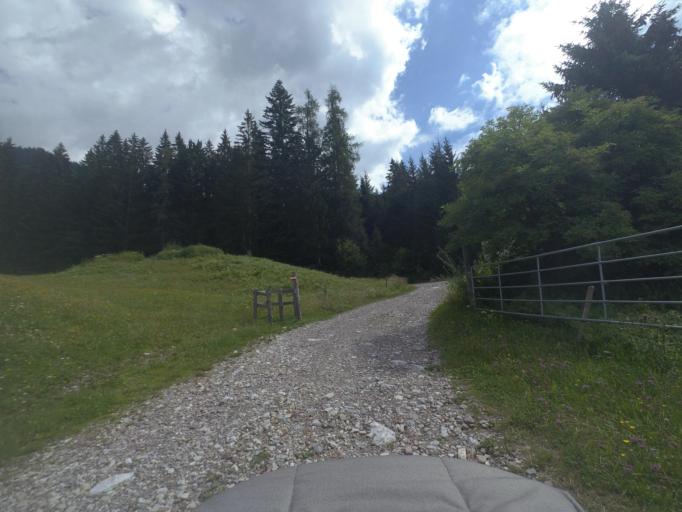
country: AT
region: Salzburg
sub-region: Politischer Bezirk Sankt Johann im Pongau
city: Werfenweng
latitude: 47.4705
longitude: 13.2413
